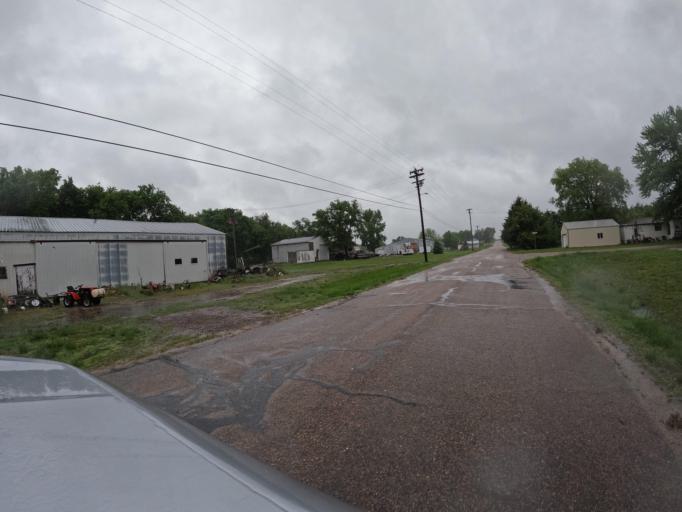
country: US
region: Nebraska
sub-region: Gage County
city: Wymore
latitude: 40.1241
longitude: -96.6575
